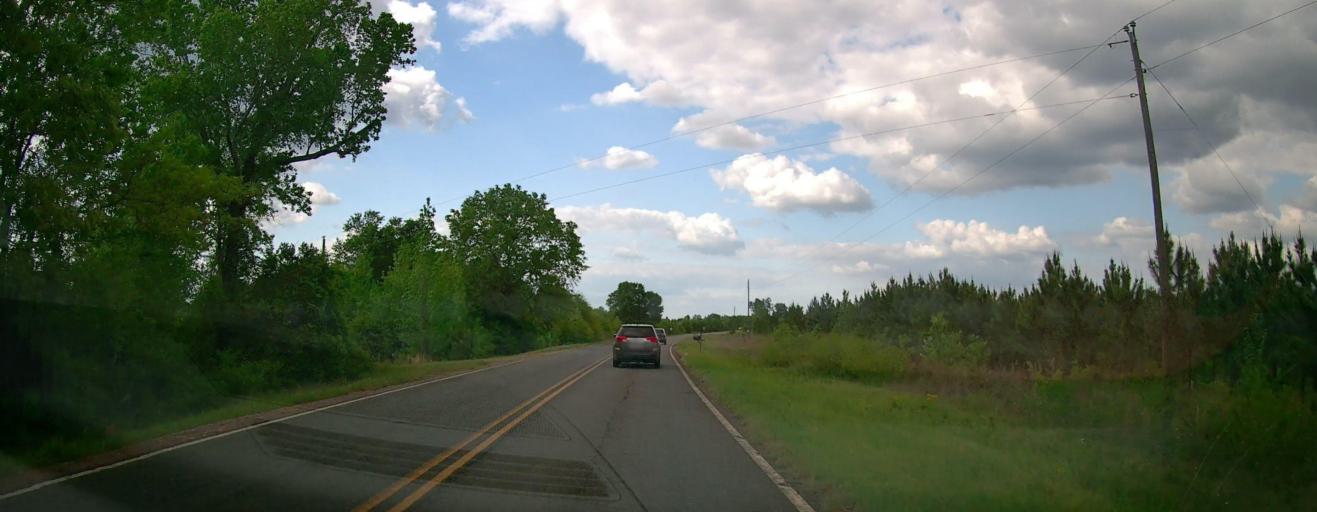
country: US
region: Georgia
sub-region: Johnson County
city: Wrightsville
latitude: 32.7598
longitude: -82.9296
